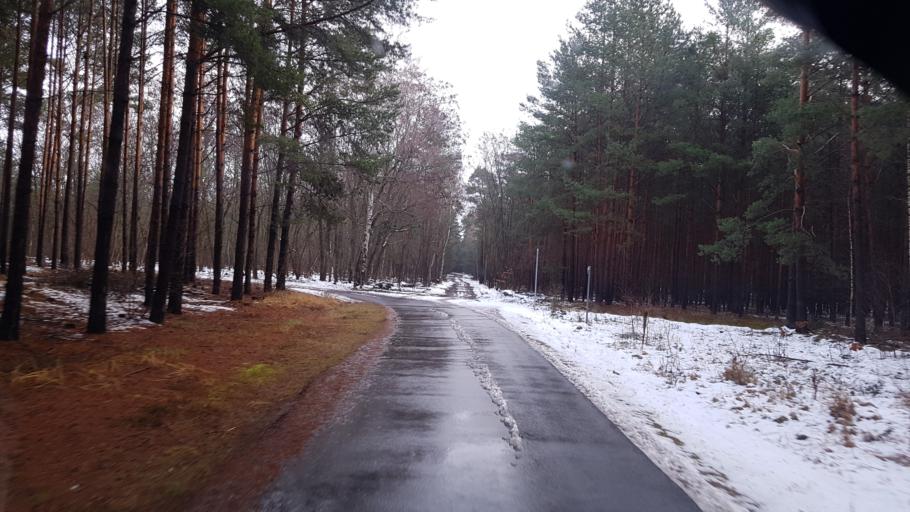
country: DE
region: Brandenburg
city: Straupitz
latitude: 51.9633
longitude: 14.1651
